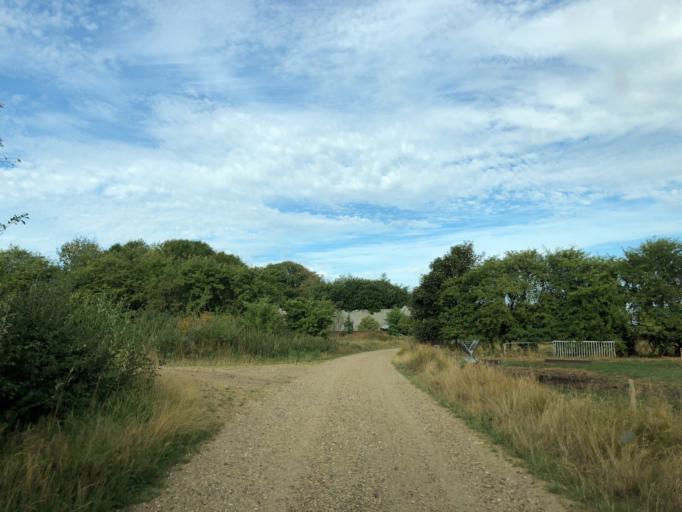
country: DK
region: Central Jutland
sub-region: Ringkobing-Skjern Kommune
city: Skjern
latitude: 56.0409
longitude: 8.4289
